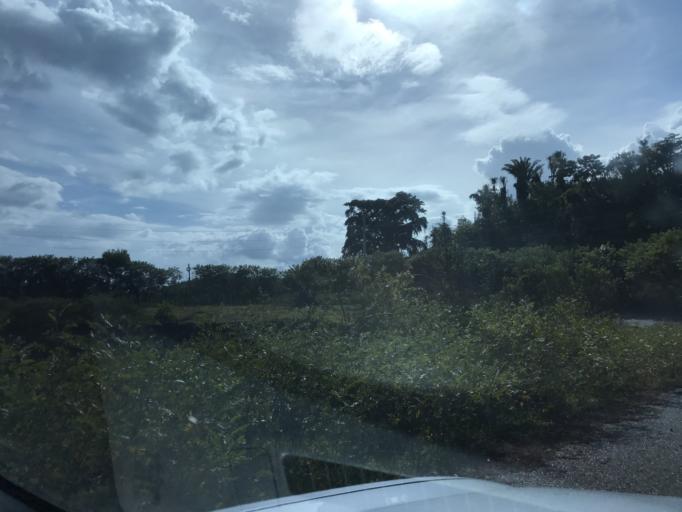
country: GT
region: Izabal
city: Morales
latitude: 15.6271
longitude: -89.0593
